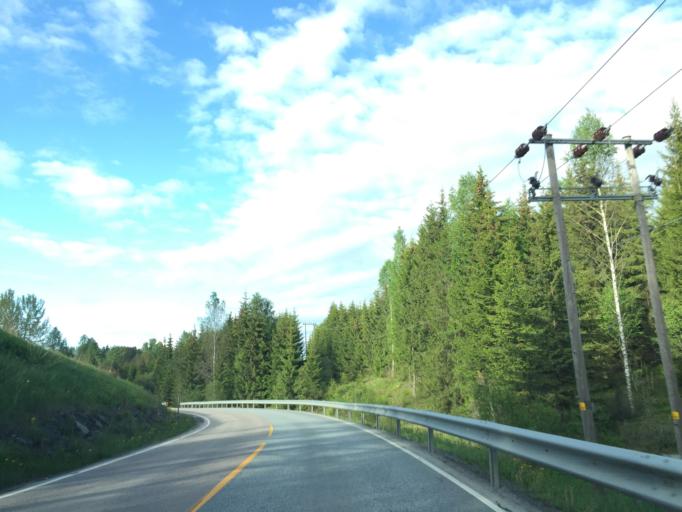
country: NO
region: Akershus
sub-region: Sorum
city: Sorumsand
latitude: 59.9892
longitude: 11.2933
